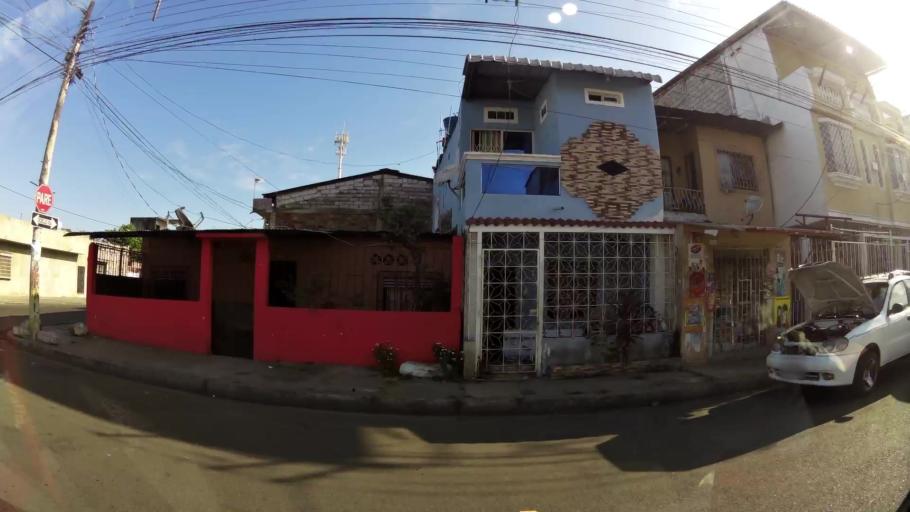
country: EC
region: Guayas
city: Guayaquil
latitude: -2.2187
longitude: -79.9197
